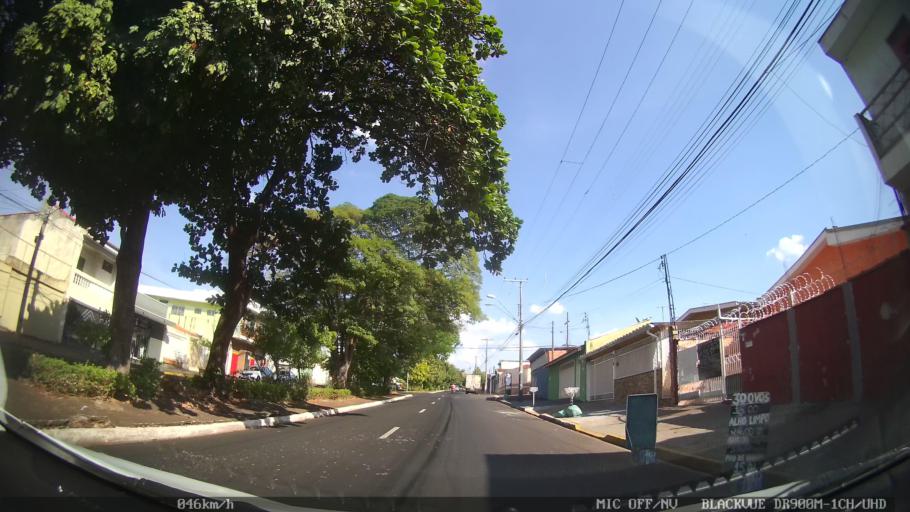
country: BR
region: Sao Paulo
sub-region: Ribeirao Preto
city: Ribeirao Preto
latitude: -21.1813
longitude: -47.8322
